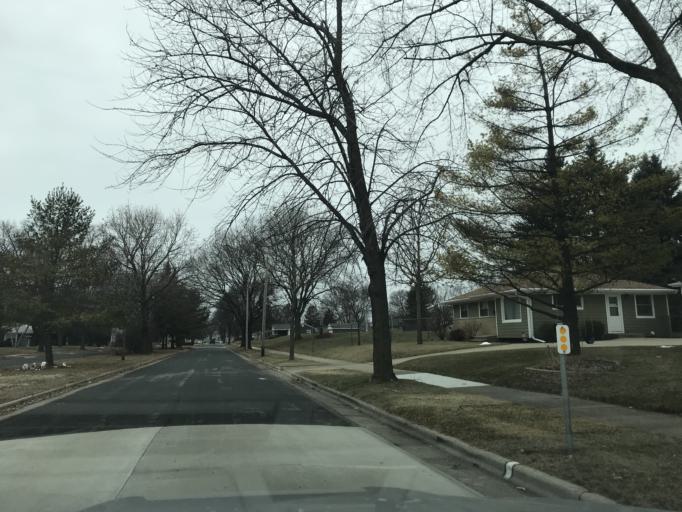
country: US
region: Wisconsin
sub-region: Dane County
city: Monona
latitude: 43.0974
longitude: -89.3104
